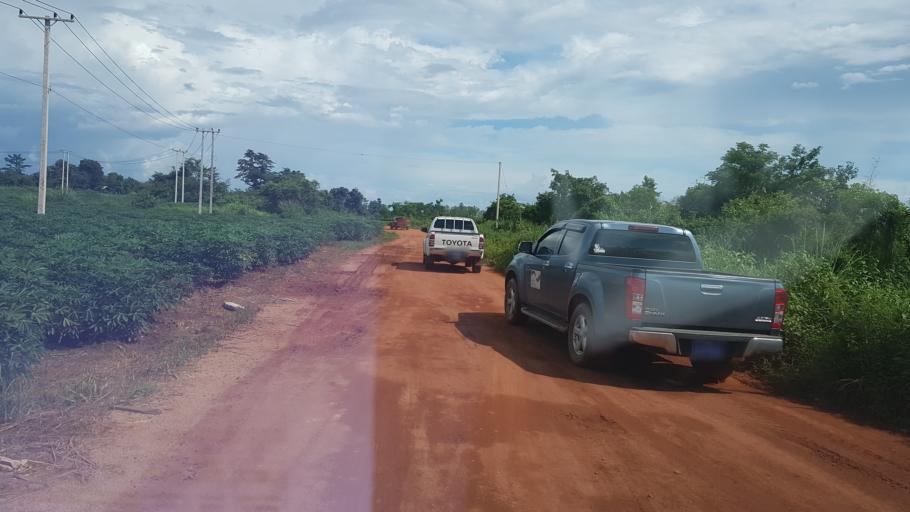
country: LA
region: Vientiane
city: Vientiane
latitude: 18.2065
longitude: 102.5679
